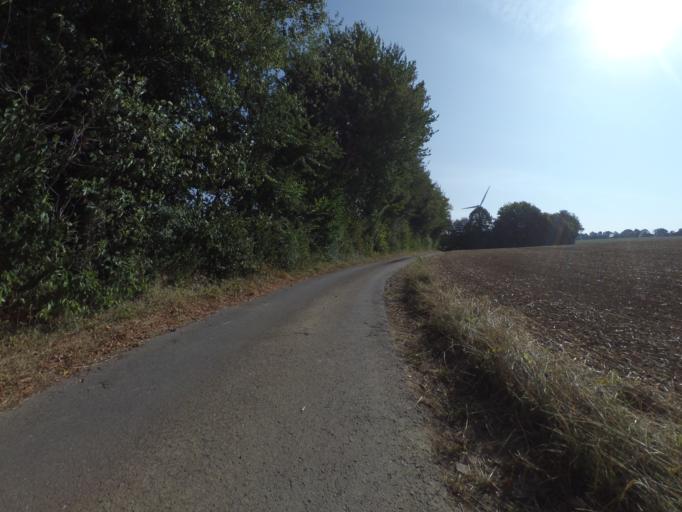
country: DE
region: Rheinland-Pfalz
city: Kirf
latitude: 49.5590
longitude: 6.4646
